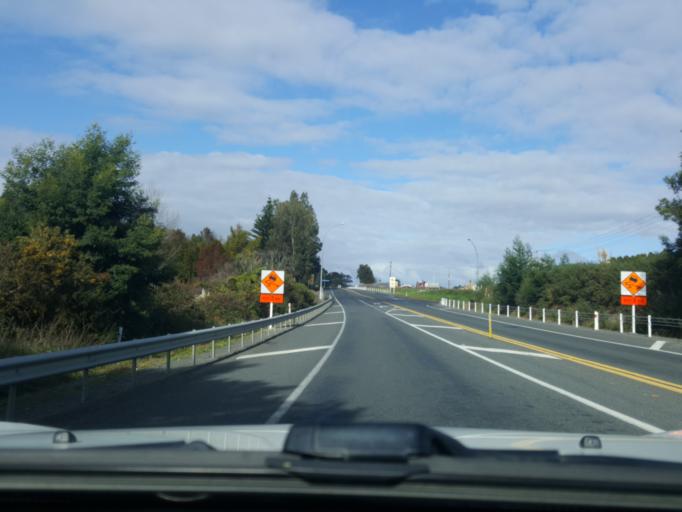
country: NZ
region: Bay of Plenty
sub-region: Western Bay of Plenty District
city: Katikati
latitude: -37.6468
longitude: 175.9660
